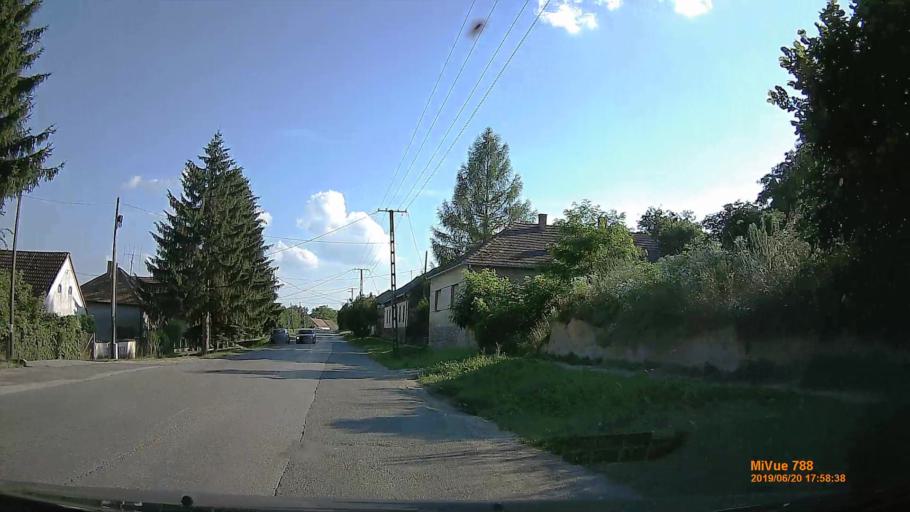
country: HU
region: Baranya
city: Buekkoesd
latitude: 46.1031
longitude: 17.9898
